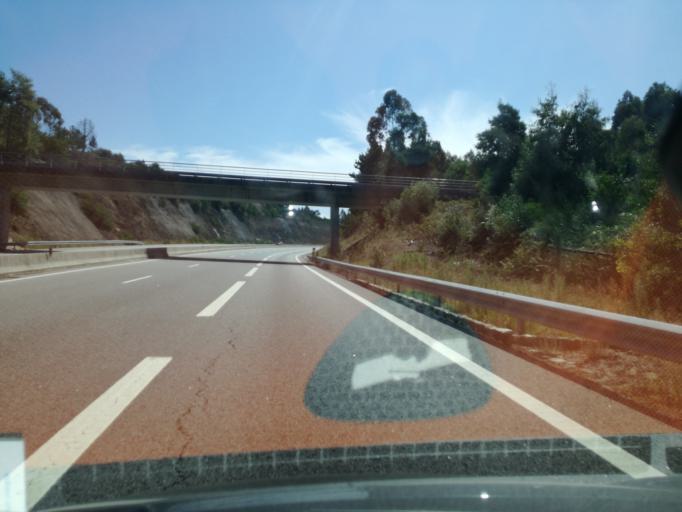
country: PT
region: Viana do Castelo
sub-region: Viana do Castelo
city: Meadela
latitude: 41.7781
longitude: -8.7854
